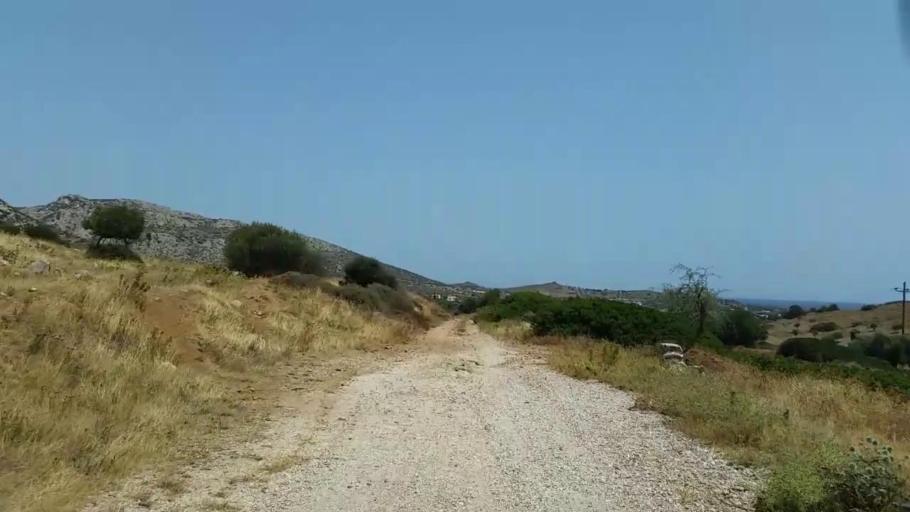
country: GR
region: Attica
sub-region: Nomarchia Anatolikis Attikis
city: Palaia Fokaia
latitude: 37.6761
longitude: 23.9587
